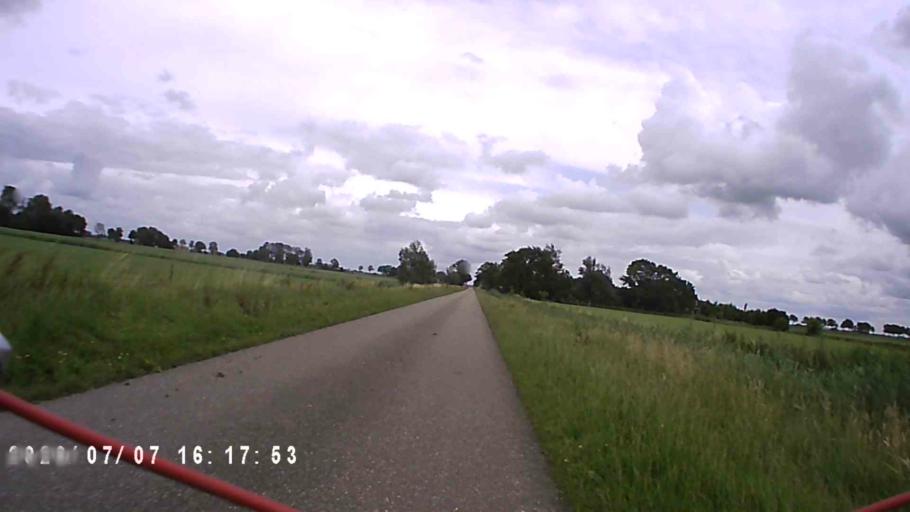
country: NL
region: Groningen
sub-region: Gemeente Winsum
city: Winsum
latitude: 53.3707
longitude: 6.5644
